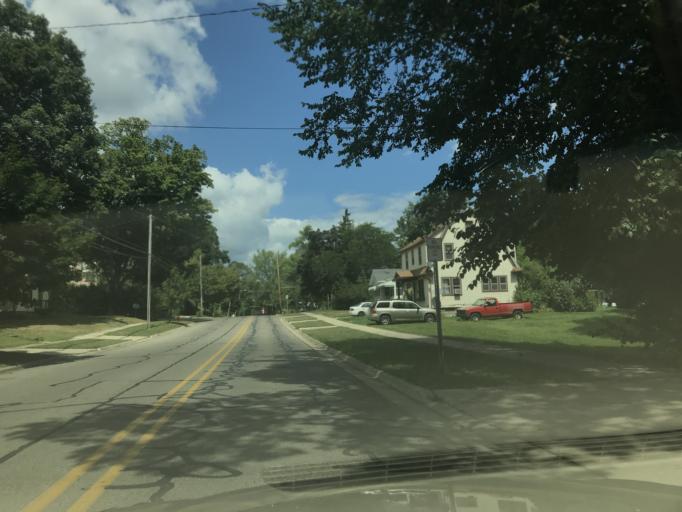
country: US
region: Michigan
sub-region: Jackson County
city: Jackson
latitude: 42.2340
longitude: -84.4184
